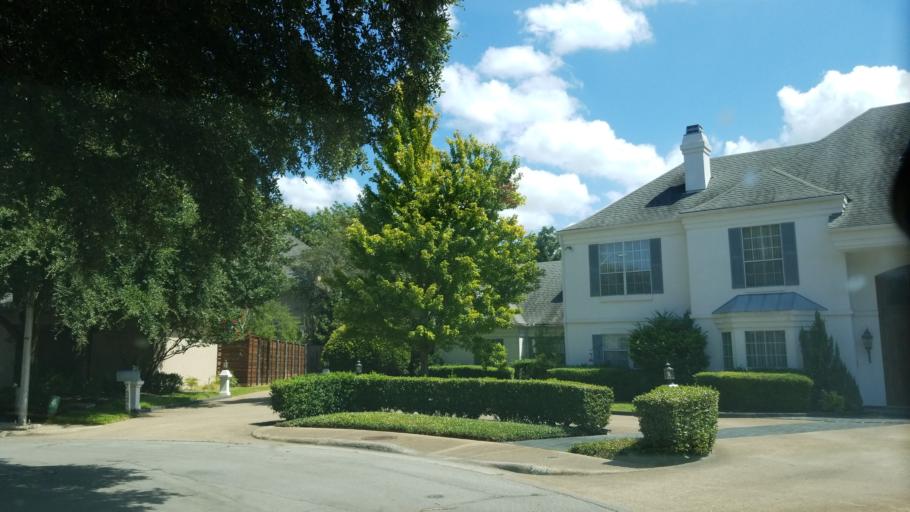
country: US
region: Texas
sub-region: Dallas County
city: Dallas
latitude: 32.7556
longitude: -96.8346
